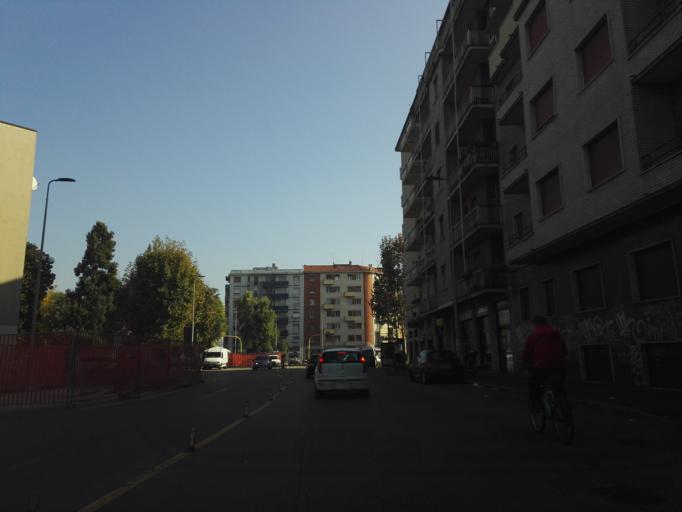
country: IT
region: Lombardy
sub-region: Citta metropolitana di Milano
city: Milano
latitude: 45.4372
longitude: 9.1967
